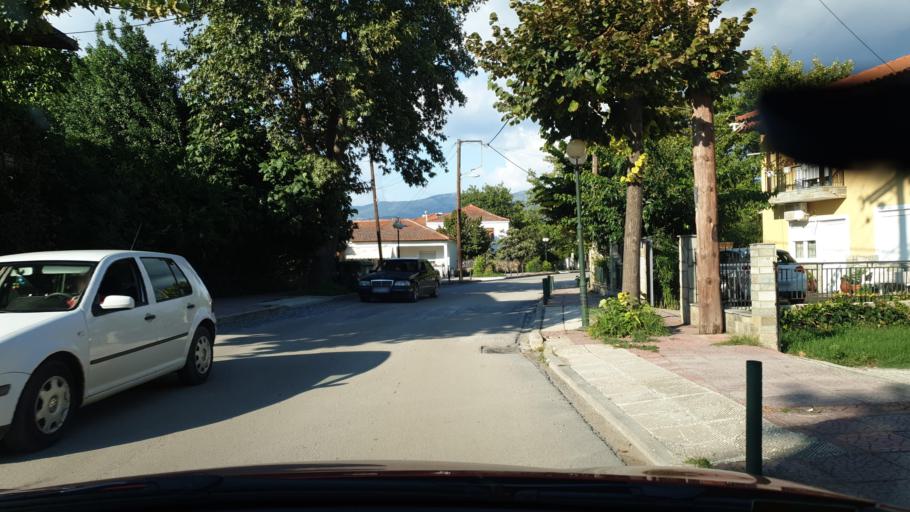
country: GR
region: Central Macedonia
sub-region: Nomos Thessalonikis
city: Vasilika
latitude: 40.4829
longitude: 23.1367
